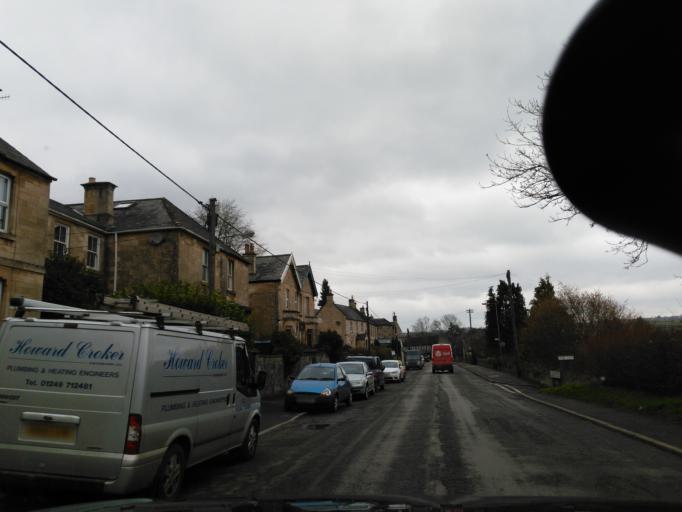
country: GB
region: England
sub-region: Wiltshire
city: Box
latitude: 51.4133
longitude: -2.2510
